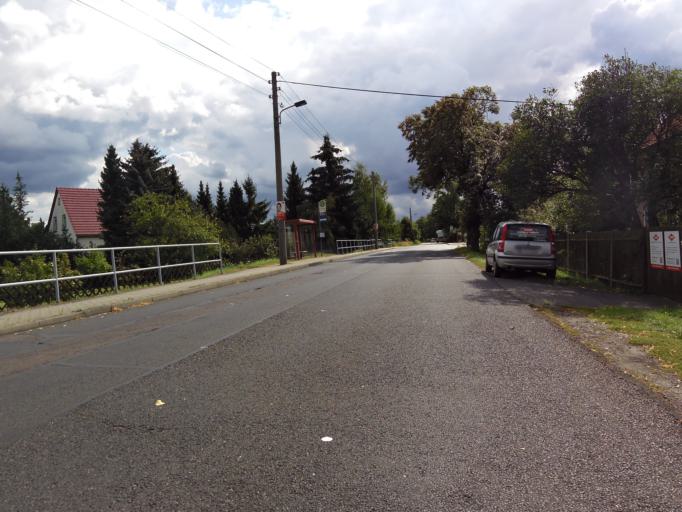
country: DE
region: Saxony
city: Rackwitz
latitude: 51.3935
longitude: 12.3397
